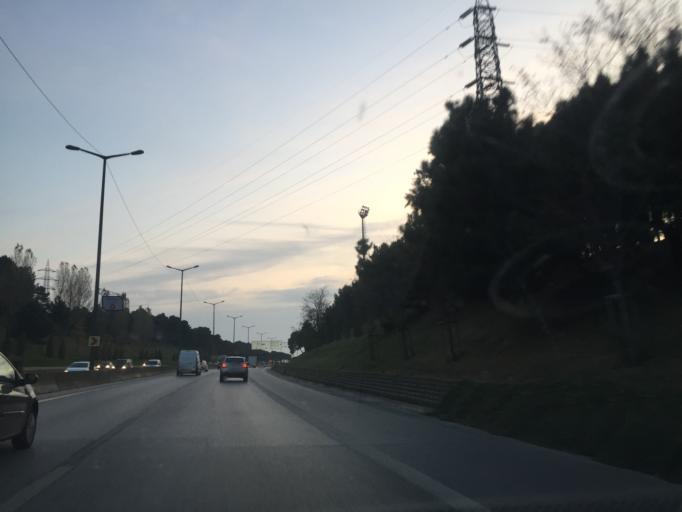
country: TR
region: Istanbul
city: Samandira
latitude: 40.9529
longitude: 29.2215
